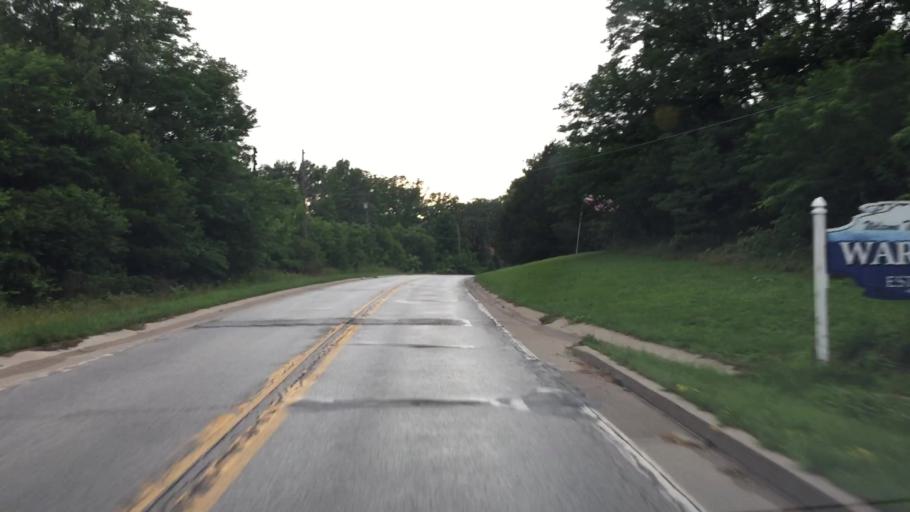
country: US
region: Illinois
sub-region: Hancock County
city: Warsaw
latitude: 40.3566
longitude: -91.4251
